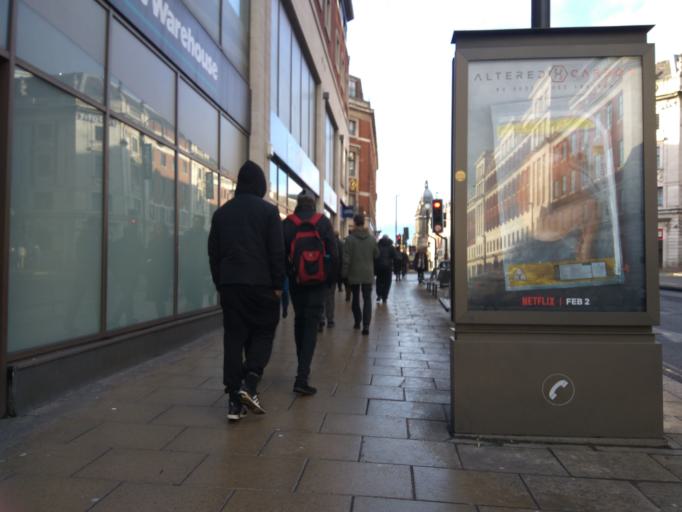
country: GB
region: England
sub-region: City and Borough of Leeds
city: Leeds
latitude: 53.7993
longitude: -1.5443
